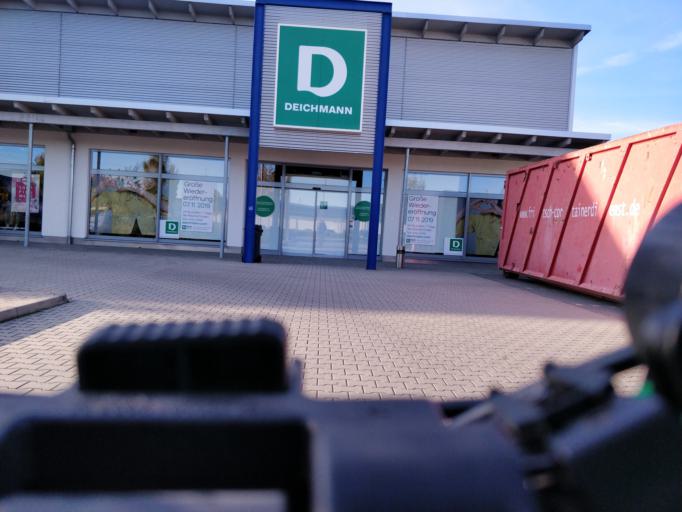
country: DE
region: Bavaria
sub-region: Swabia
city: Mering
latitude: 48.2746
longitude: 10.9739
